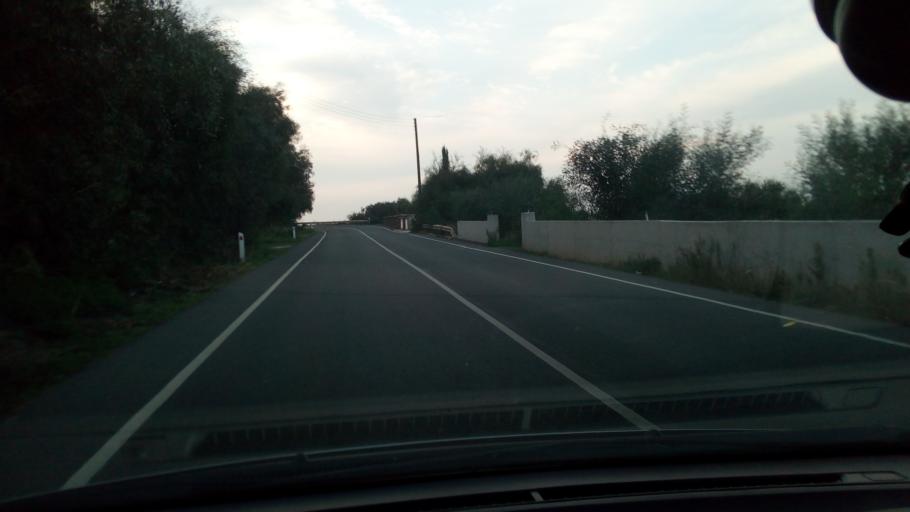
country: CY
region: Lefkosia
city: Kato Pyrgos
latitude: 35.1488
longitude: 32.5357
